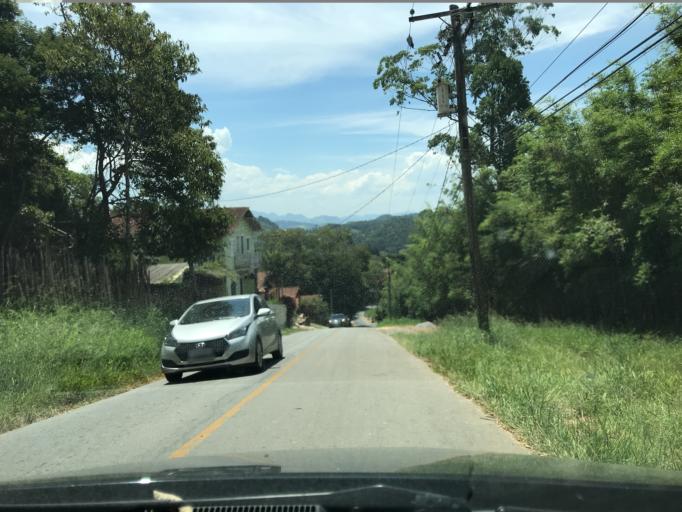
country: BR
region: Sao Paulo
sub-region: Campos Do Jordao
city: Campos do Jordao
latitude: -22.8323
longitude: -45.6659
